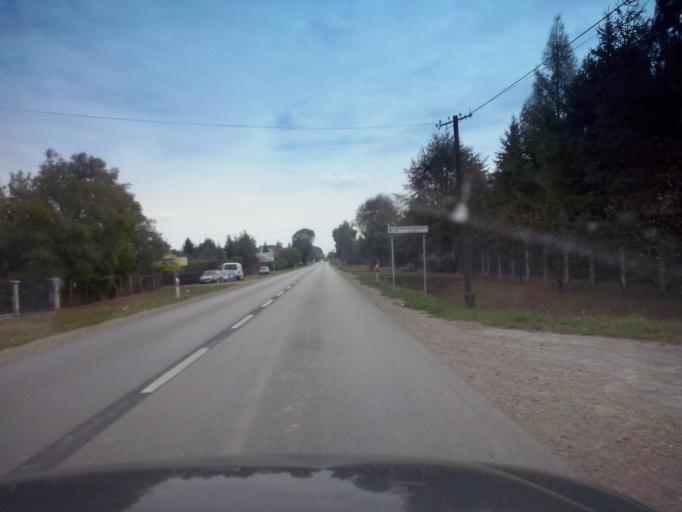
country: PL
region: Subcarpathian Voivodeship
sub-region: Powiat stalowowolski
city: Stalowa Wola
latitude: 50.6058
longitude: 22.0175
